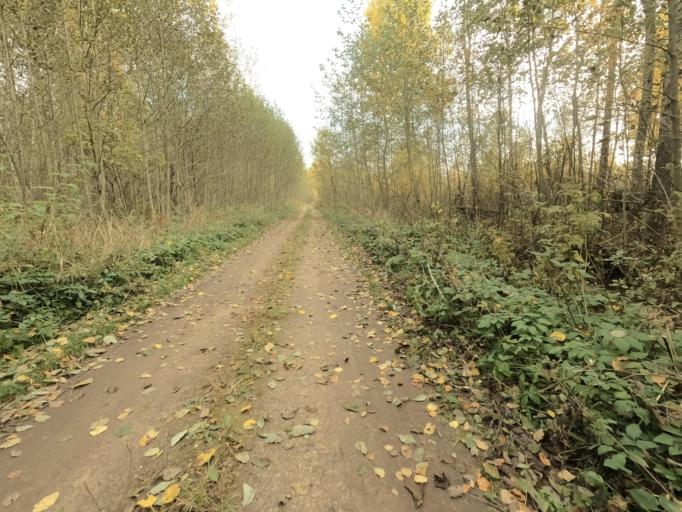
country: RU
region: Novgorod
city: Pankovka
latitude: 58.8802
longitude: 30.8440
